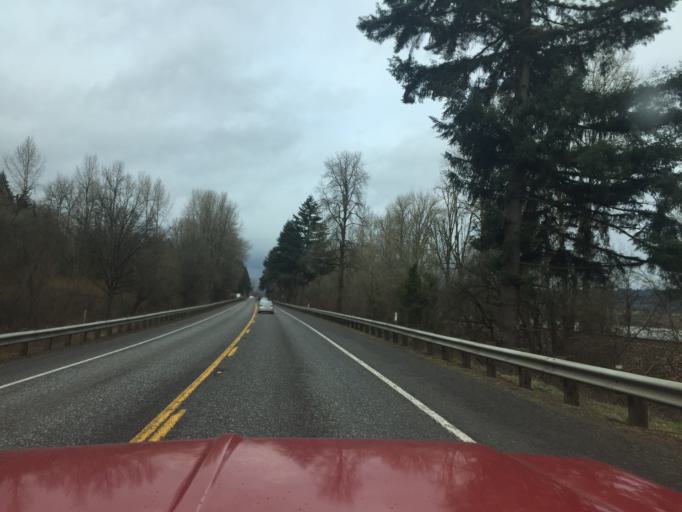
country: US
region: Washington
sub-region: Cowlitz County
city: Kalama
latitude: 46.0102
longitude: -122.8748
